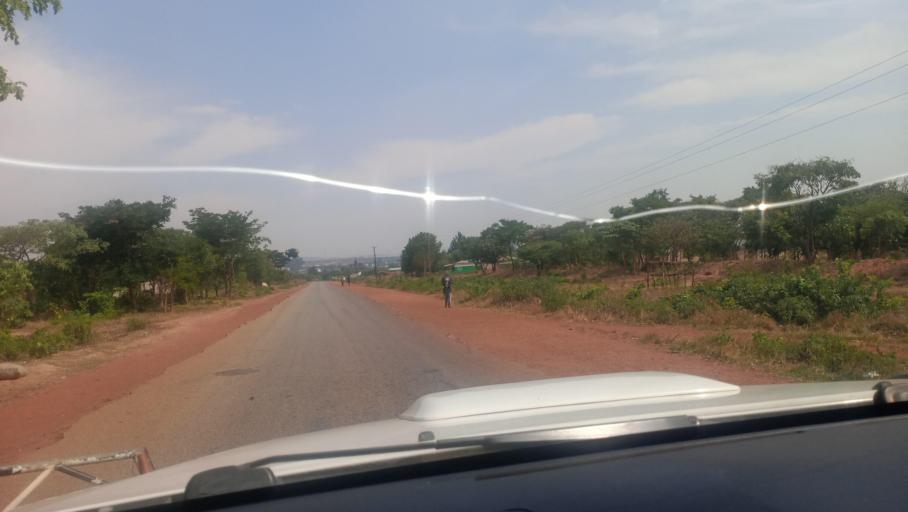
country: ZM
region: Northern
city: Mpika
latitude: -11.8317
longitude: 31.3792
